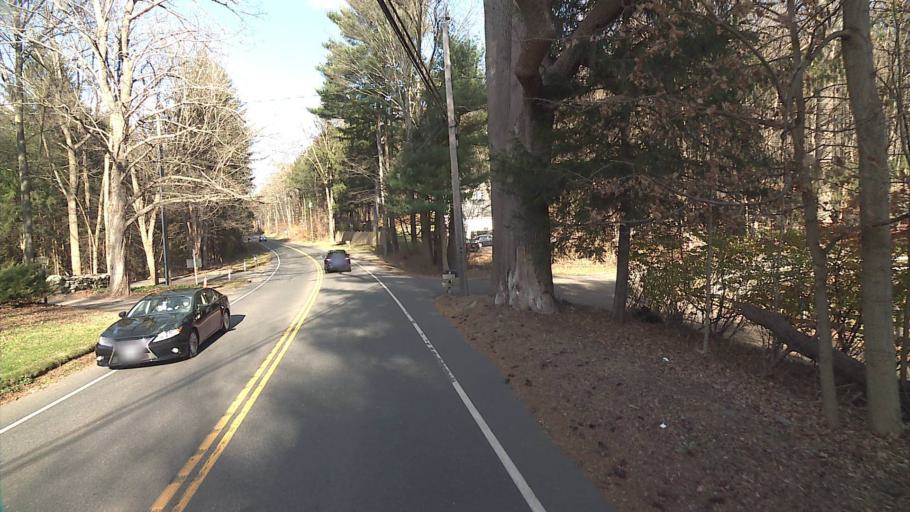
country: US
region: Connecticut
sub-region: Fairfield County
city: Bethel
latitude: 41.3463
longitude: -73.4143
